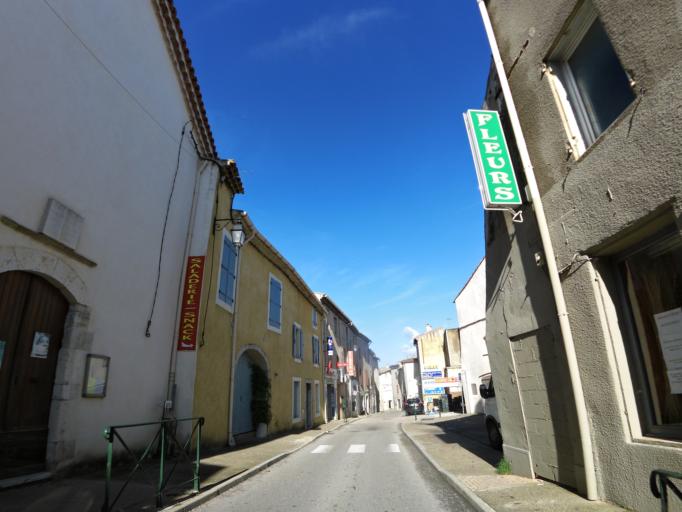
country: FR
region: Languedoc-Roussillon
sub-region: Departement du Gard
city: Ledignan
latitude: 43.9890
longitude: 4.1067
